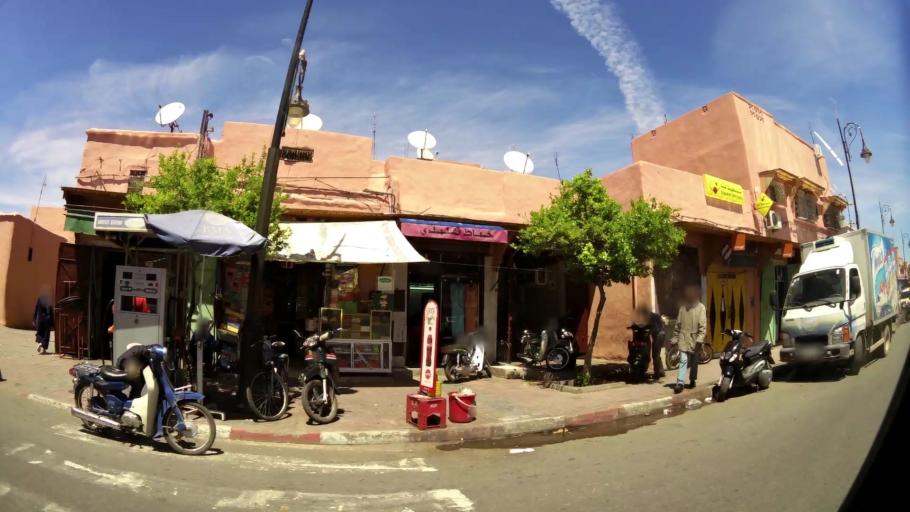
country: MA
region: Marrakech-Tensift-Al Haouz
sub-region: Marrakech
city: Marrakesh
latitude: 31.6143
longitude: -7.9793
